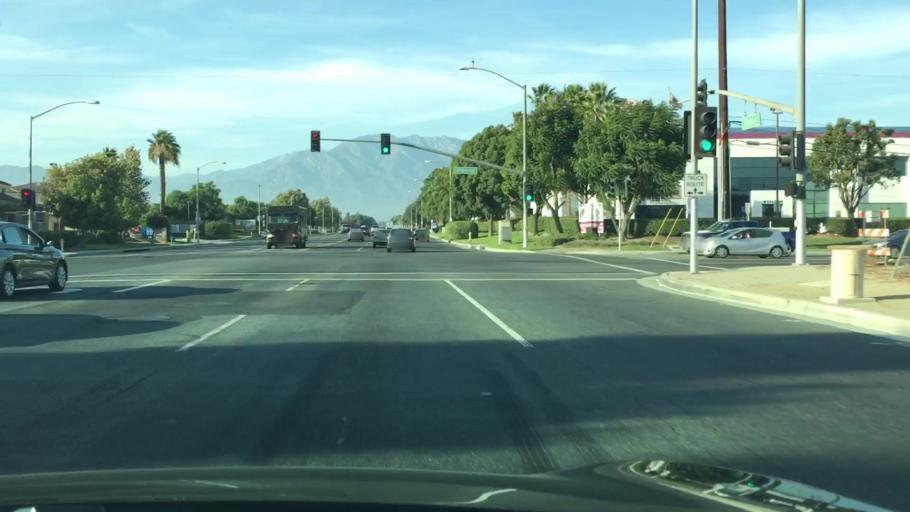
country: US
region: California
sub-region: San Bernardino County
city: Ontario
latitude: 34.0409
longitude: -117.6285
